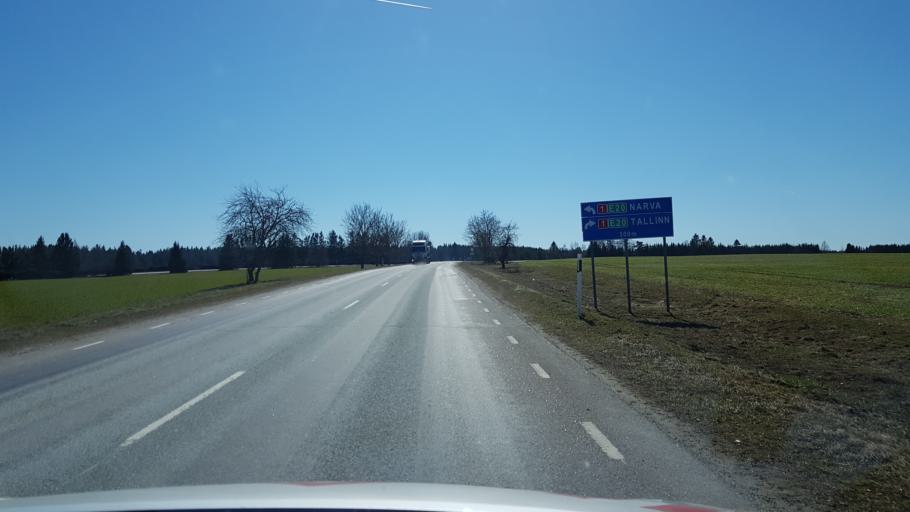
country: EE
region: Ida-Virumaa
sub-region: Aseri vald
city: Aseri
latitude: 59.4331
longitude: 26.6983
